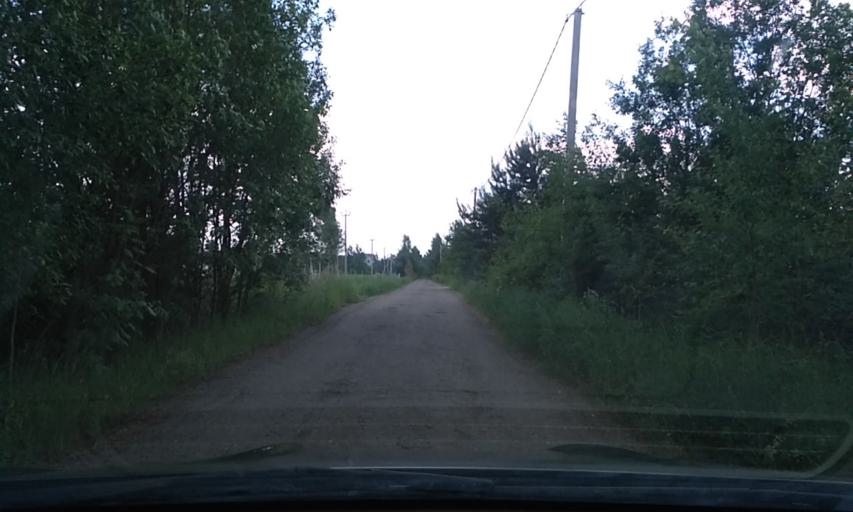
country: RU
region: Leningrad
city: Otradnoye
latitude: 59.8093
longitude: 30.8271
